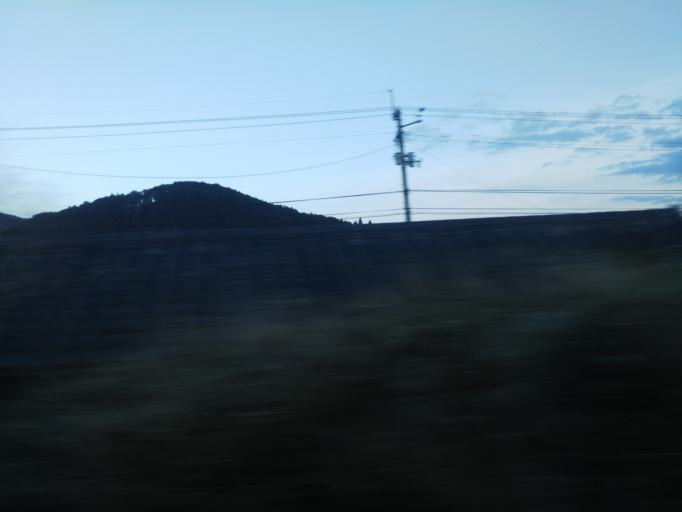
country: JP
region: Kochi
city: Susaki
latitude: 33.2402
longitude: 133.1576
